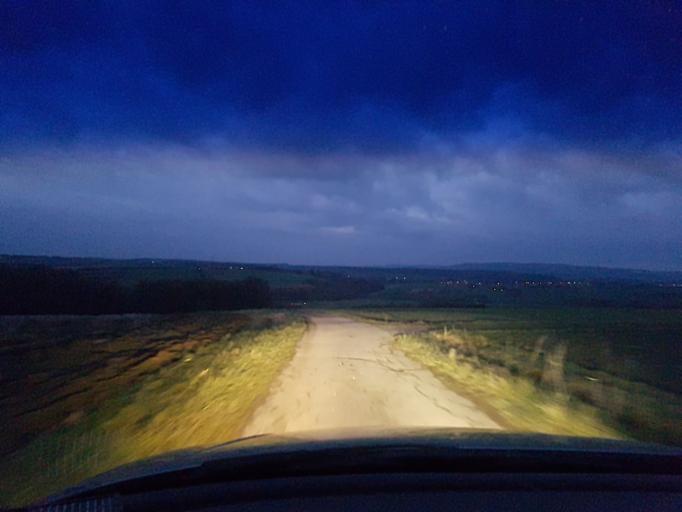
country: DE
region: Bavaria
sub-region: Upper Franconia
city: Memmelsdorf
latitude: 49.9366
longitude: 10.9837
